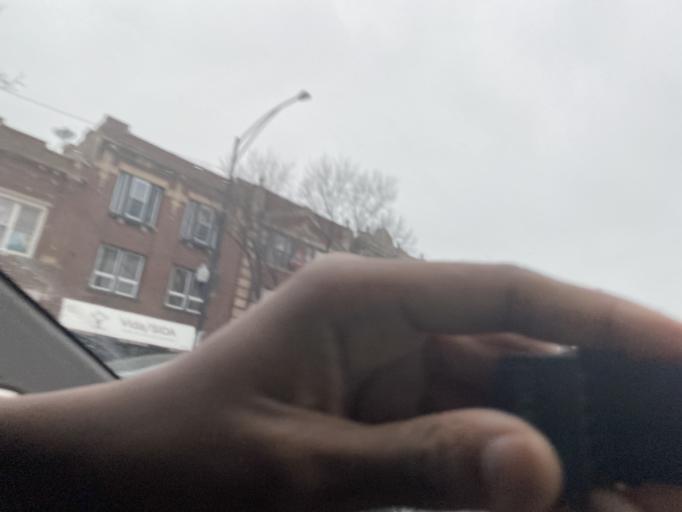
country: US
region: Illinois
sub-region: Cook County
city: Chicago
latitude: 41.9029
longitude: -87.6937
